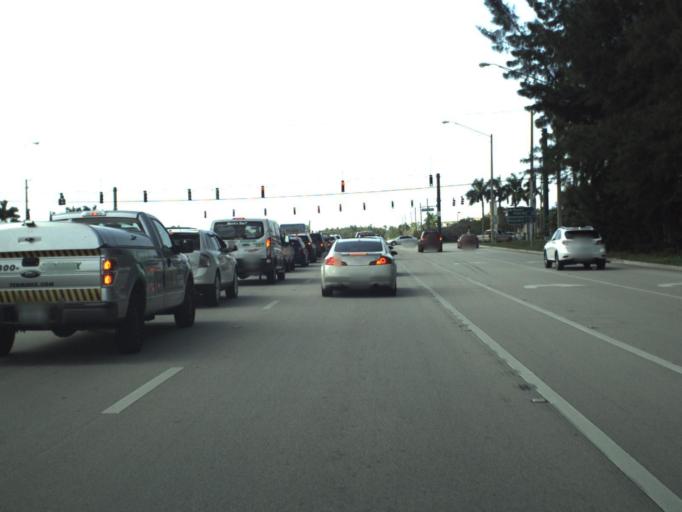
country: US
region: Florida
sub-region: Palm Beach County
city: Royal Palm Beach
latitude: 26.7080
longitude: -80.2008
